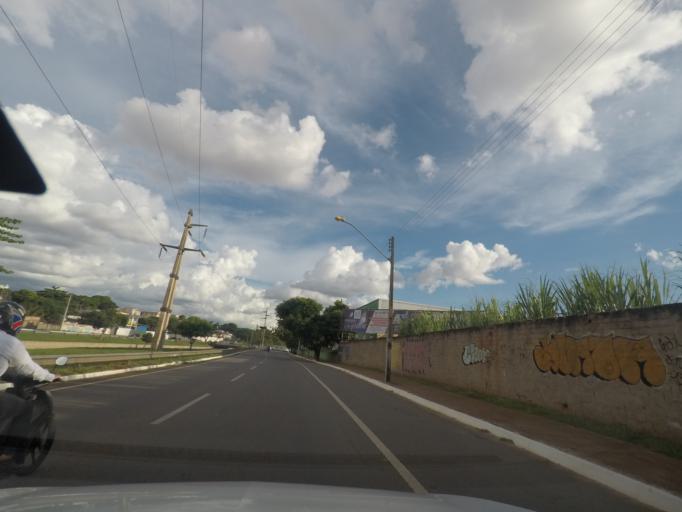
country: BR
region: Goias
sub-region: Goiania
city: Goiania
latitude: -16.6834
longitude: -49.2927
